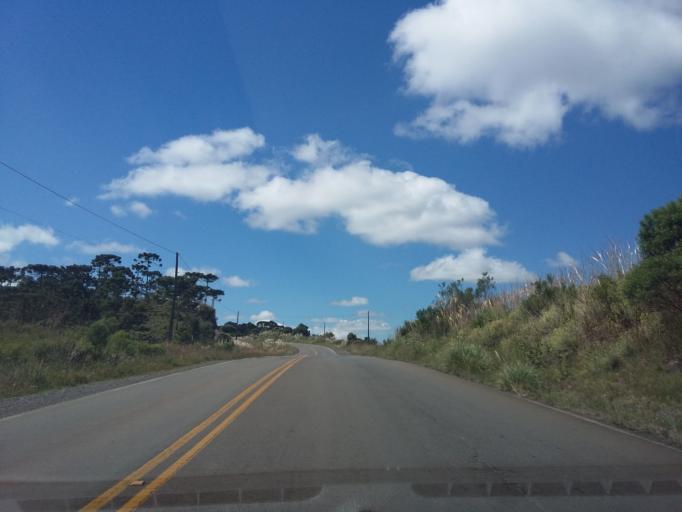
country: BR
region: Santa Catarina
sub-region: Sao Joaquim
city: Sao Joaquim
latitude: -28.2832
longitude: -49.7544
